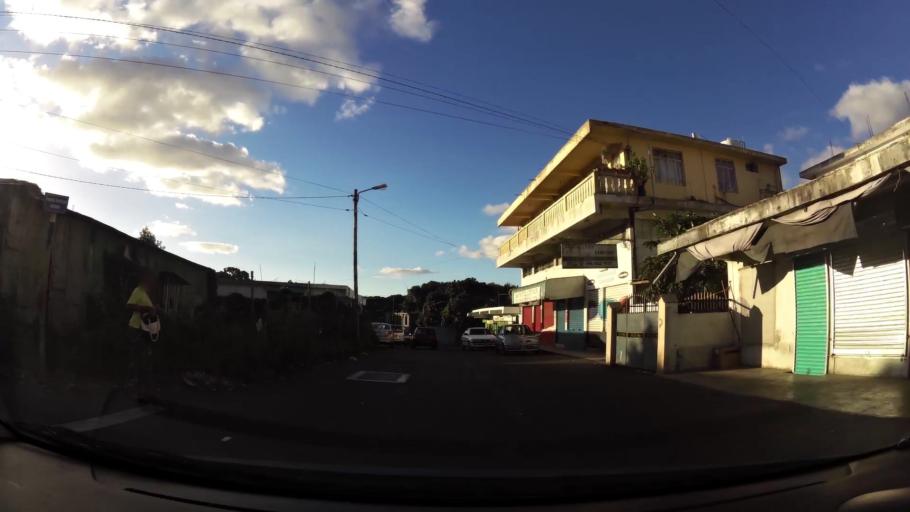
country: MU
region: Plaines Wilhems
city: Quatre Bornes
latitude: -20.2454
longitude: 57.4617
